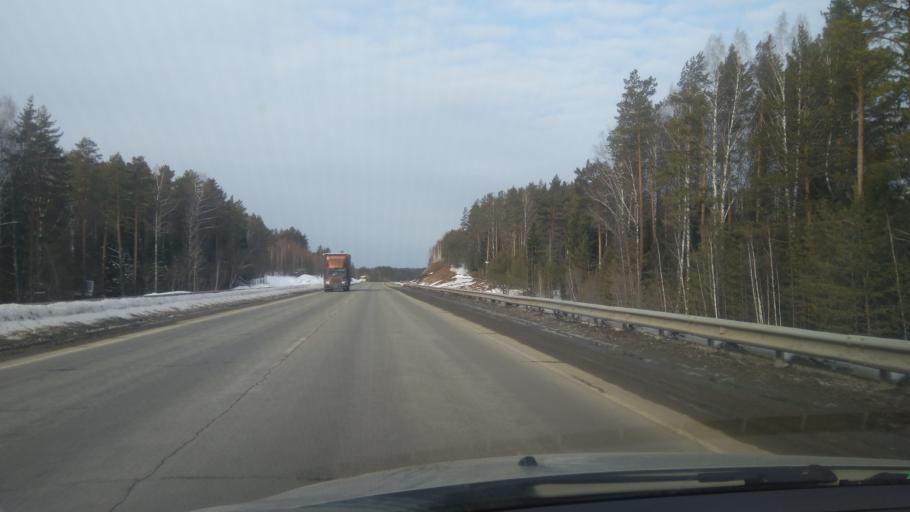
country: RU
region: Sverdlovsk
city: Bisert'
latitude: 56.8272
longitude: 58.9895
